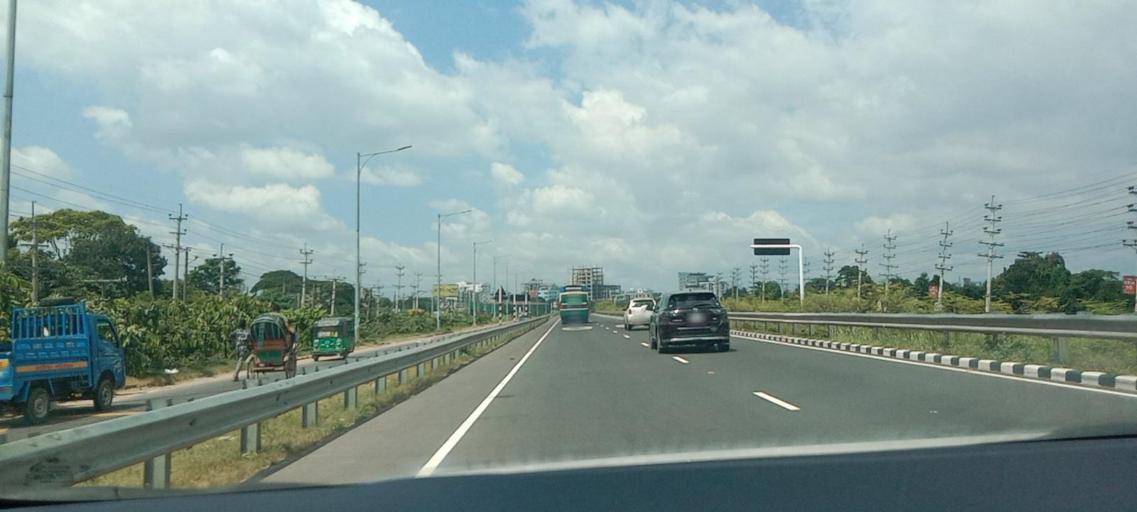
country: BD
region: Dhaka
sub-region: Dhaka
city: Dhaka
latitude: 23.6797
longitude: 90.4110
